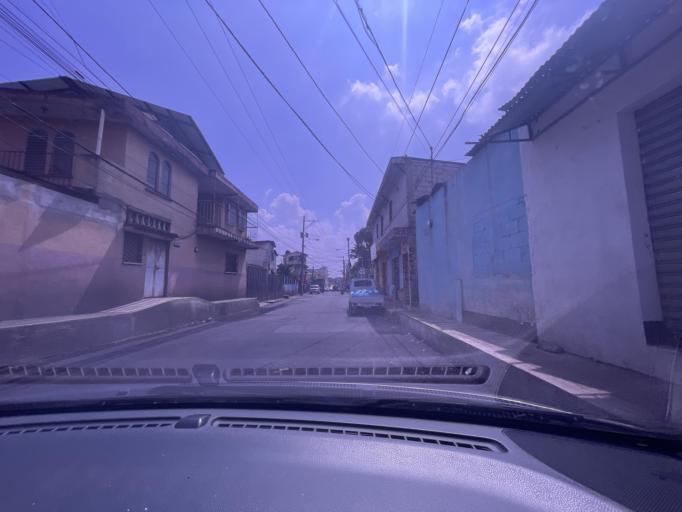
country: GT
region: Guatemala
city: Guatemala City
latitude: 14.6727
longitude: -90.5457
